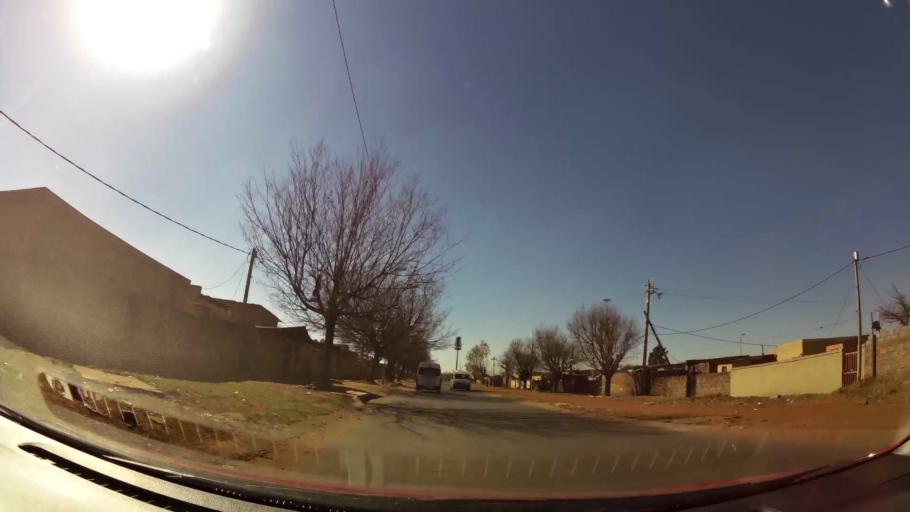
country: ZA
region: Gauteng
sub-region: City of Johannesburg Metropolitan Municipality
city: Soweto
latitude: -26.2254
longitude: 27.8244
